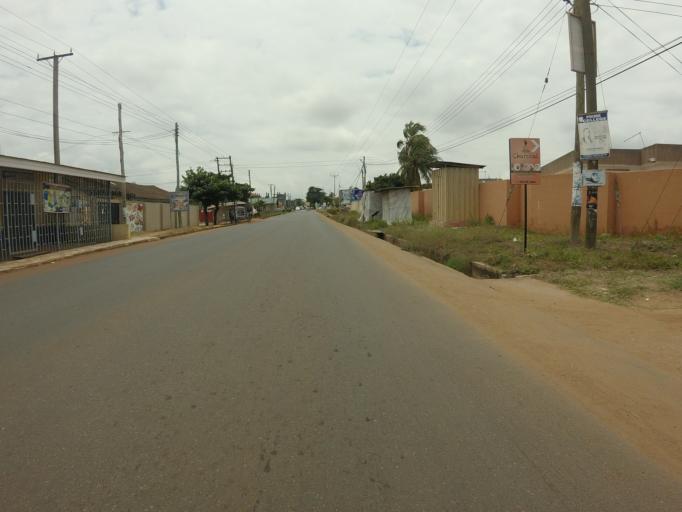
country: GH
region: Greater Accra
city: Nungua
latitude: 5.6050
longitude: -0.0931
